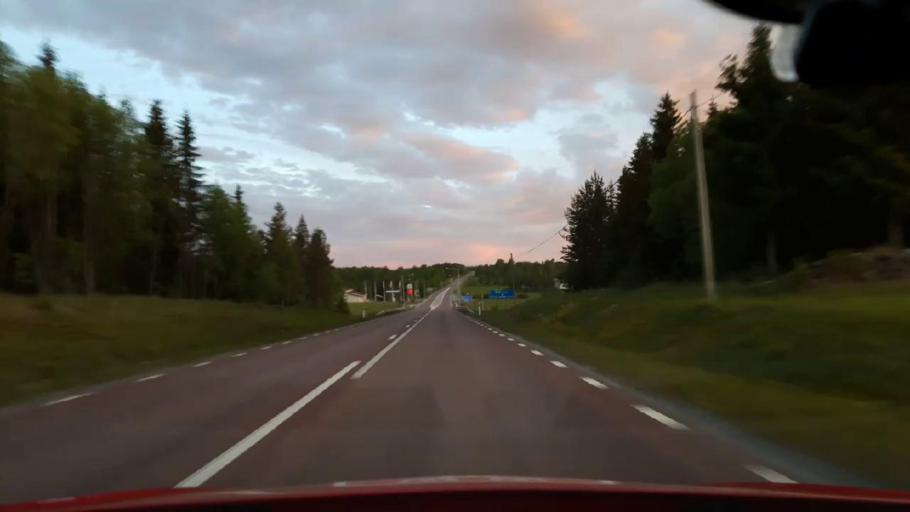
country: SE
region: Jaemtland
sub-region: OEstersunds Kommun
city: Ostersund
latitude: 62.9928
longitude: 14.6035
